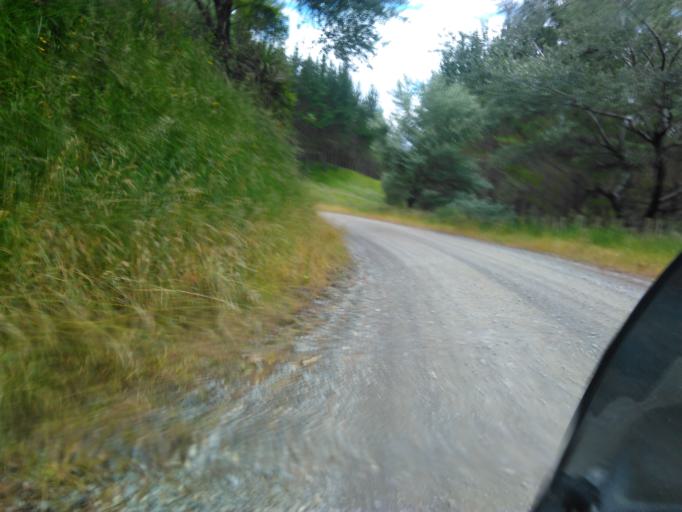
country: NZ
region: Gisborne
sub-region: Gisborne District
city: Gisborne
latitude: -38.0595
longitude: 178.1545
